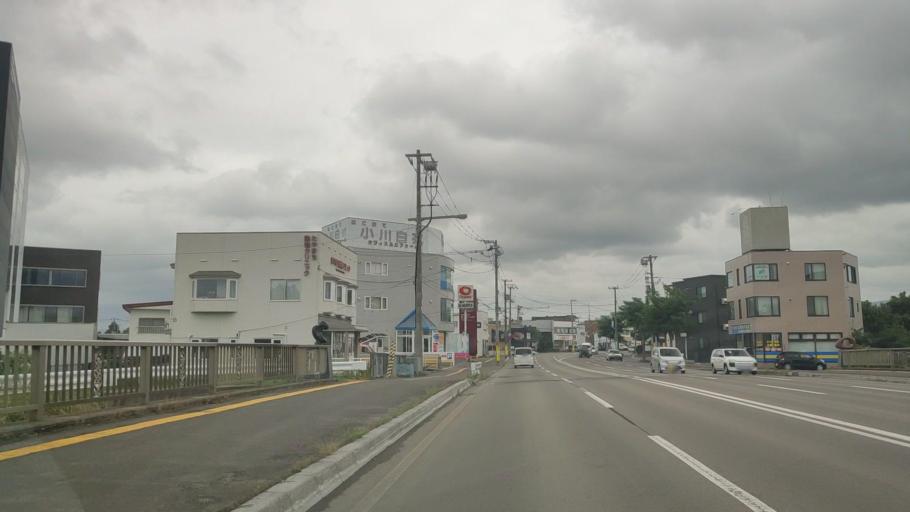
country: JP
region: Hokkaido
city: Hakodate
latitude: 41.7981
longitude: 140.7508
